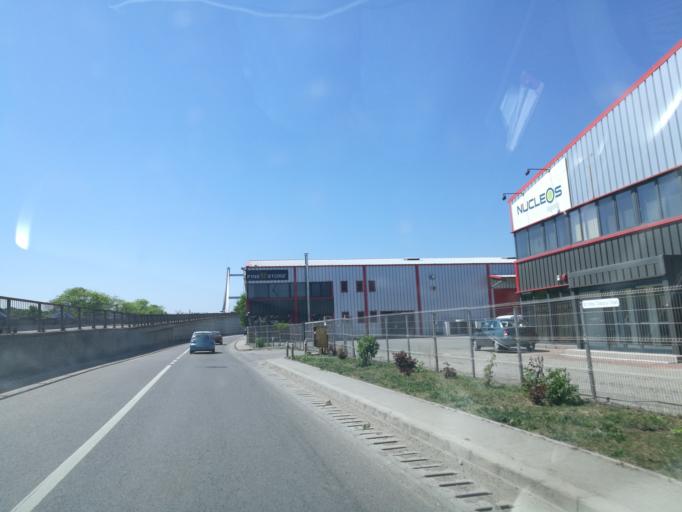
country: RO
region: Ilfov
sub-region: Comuna Otopeni
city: Otopeni
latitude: 44.5377
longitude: 26.0814
